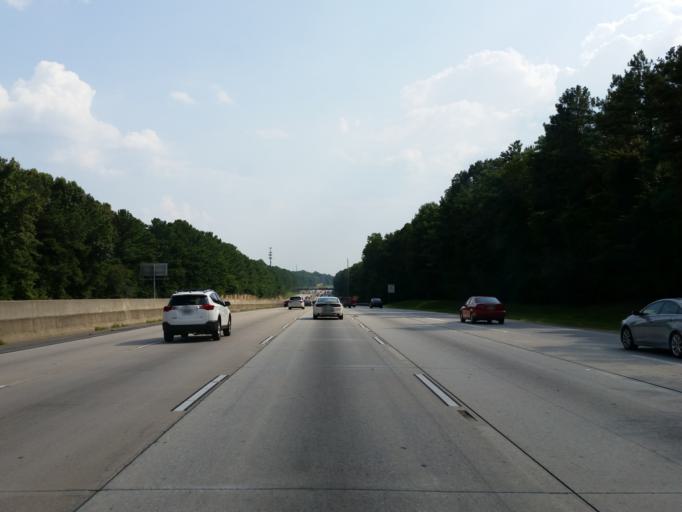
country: US
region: Georgia
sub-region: DeKalb County
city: Dunwoody
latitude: 33.9776
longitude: -84.3442
